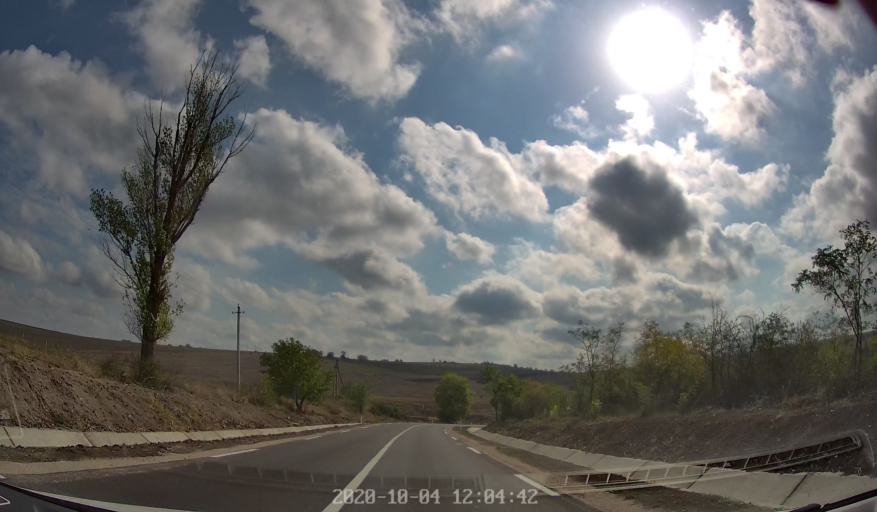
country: MD
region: Rezina
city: Saharna
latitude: 47.6017
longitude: 28.9462
